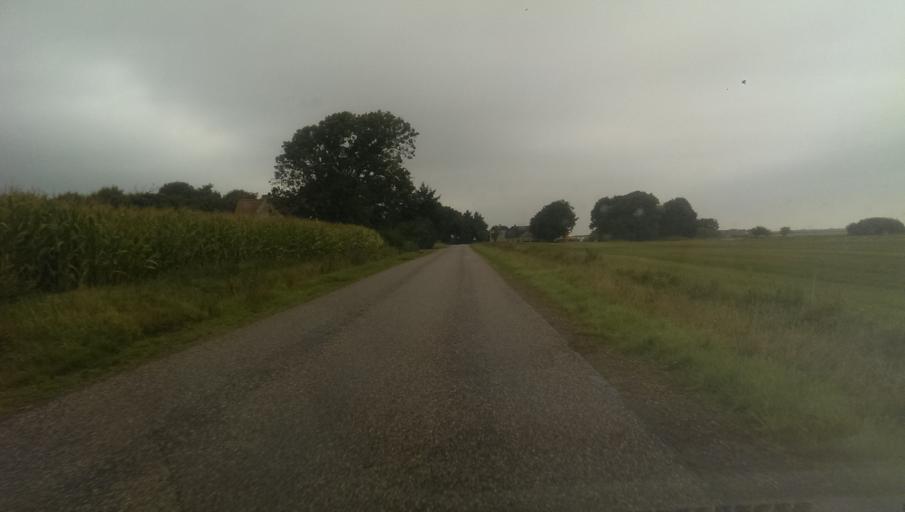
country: DK
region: South Denmark
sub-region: Esbjerg Kommune
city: Tjaereborg
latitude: 55.5098
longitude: 8.5314
